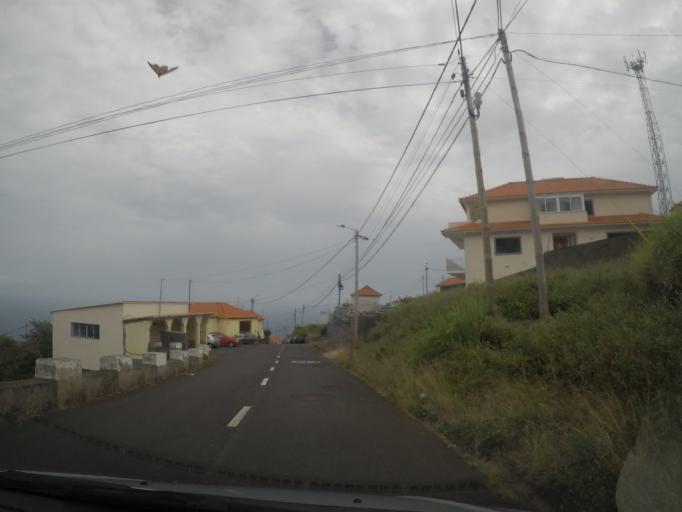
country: PT
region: Madeira
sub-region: Santa Cruz
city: Santa Cruz
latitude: 32.6845
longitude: -16.8100
